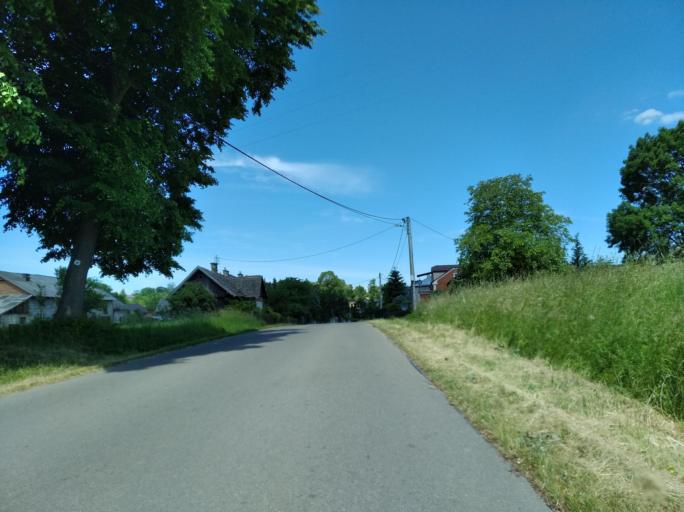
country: PL
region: Subcarpathian Voivodeship
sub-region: Powiat jasielski
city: Osiek Jasielski
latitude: 49.6647
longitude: 21.5430
